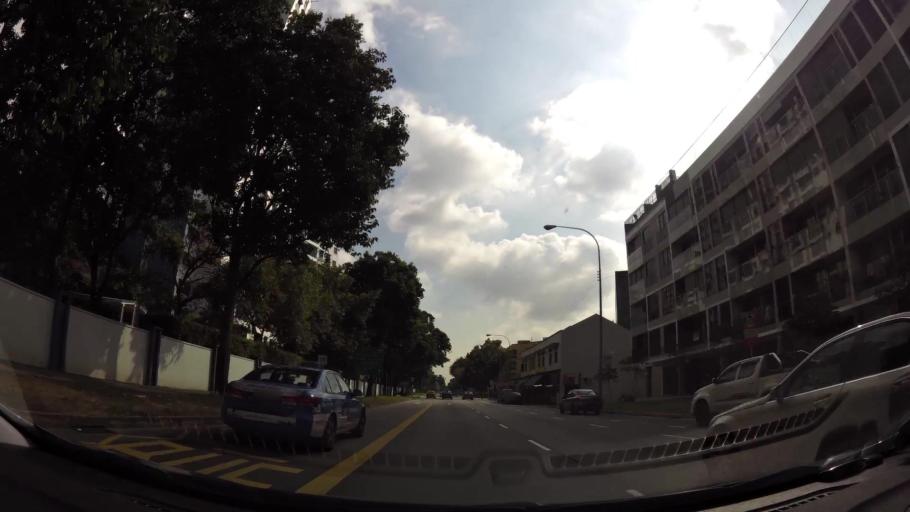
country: SG
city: Singapore
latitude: 1.3154
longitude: 103.8840
